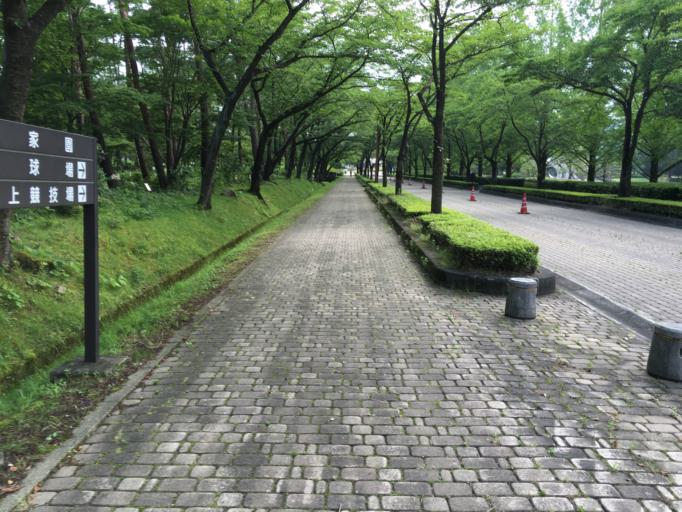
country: JP
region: Fukushima
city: Fukushima-shi
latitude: 37.7243
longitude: 140.3667
